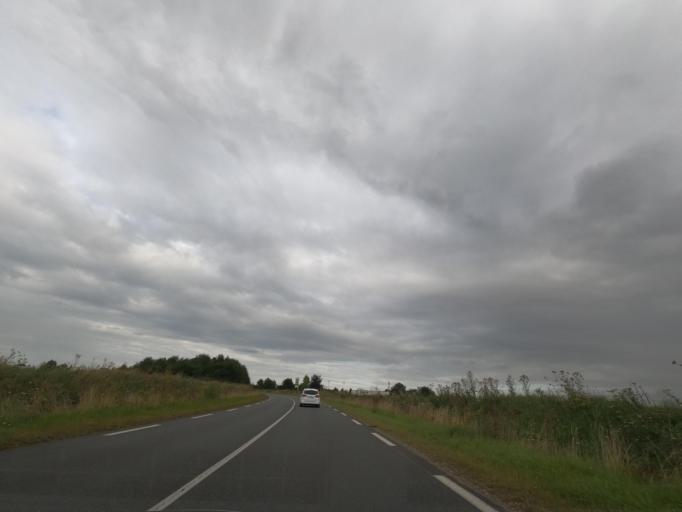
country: FR
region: Haute-Normandie
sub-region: Departement de l'Eure
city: Bourgtheroulde-Infreville
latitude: 49.2918
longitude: 0.8719
